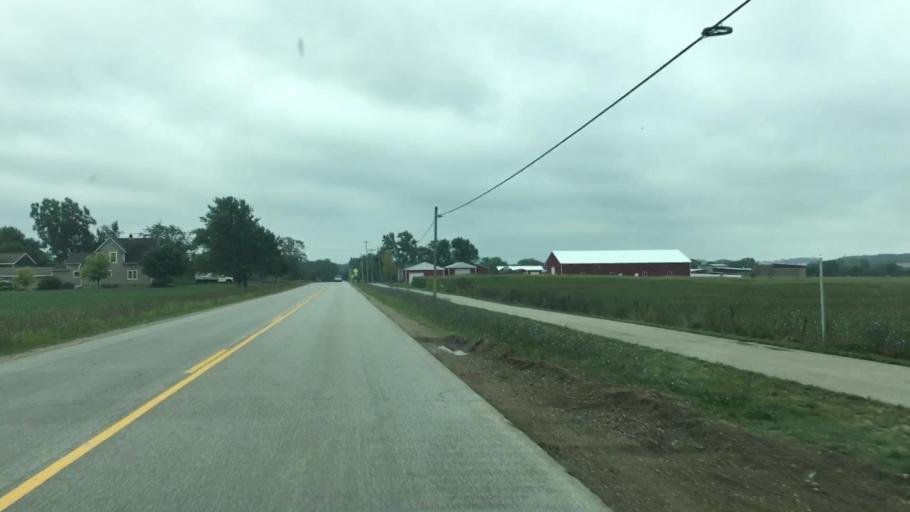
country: US
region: Michigan
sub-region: Ottawa County
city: Hudsonville
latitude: 42.8363
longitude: -85.8421
